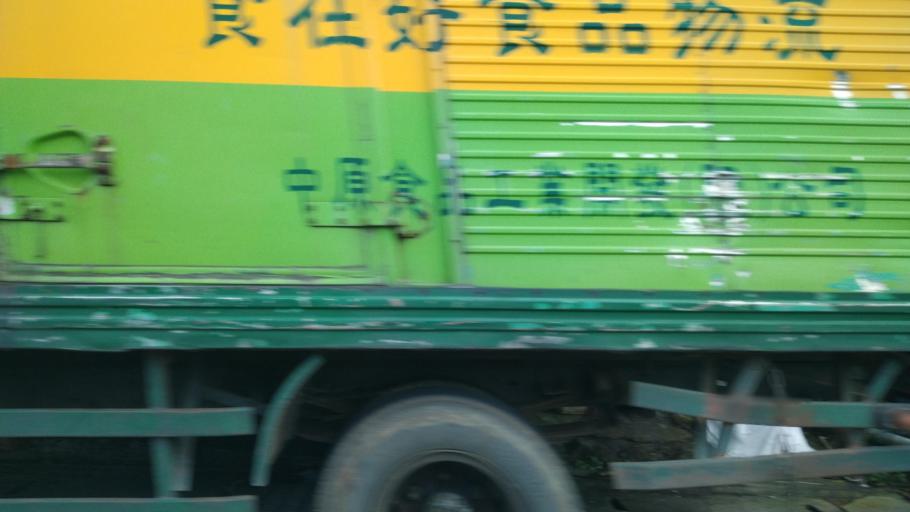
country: TW
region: Taiwan
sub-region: Taoyuan
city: Taoyuan
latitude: 24.9200
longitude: 121.3691
